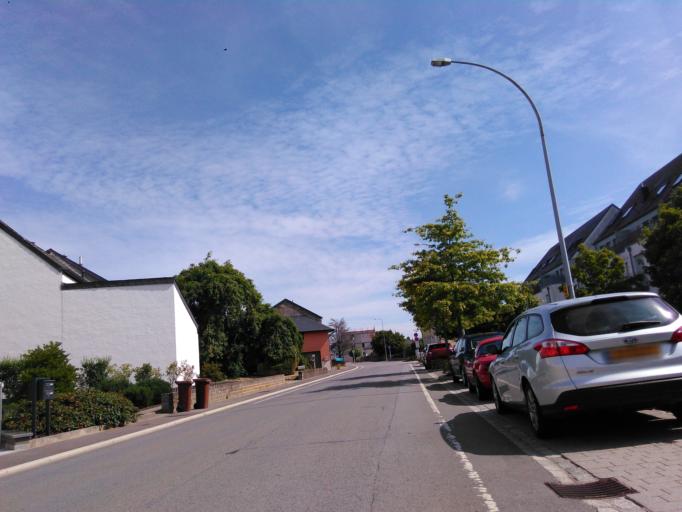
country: LU
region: Luxembourg
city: Fentange
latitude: 49.5619
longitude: 6.1496
